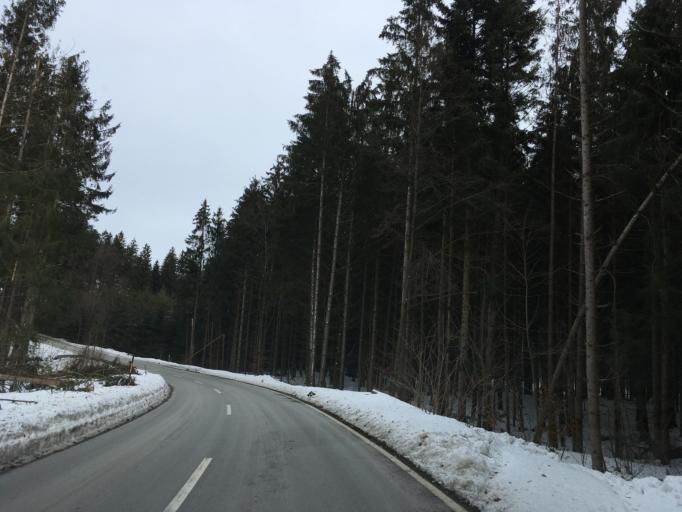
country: DE
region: Bavaria
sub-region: Upper Bavaria
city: Schnaitsee
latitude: 48.0559
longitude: 12.3525
